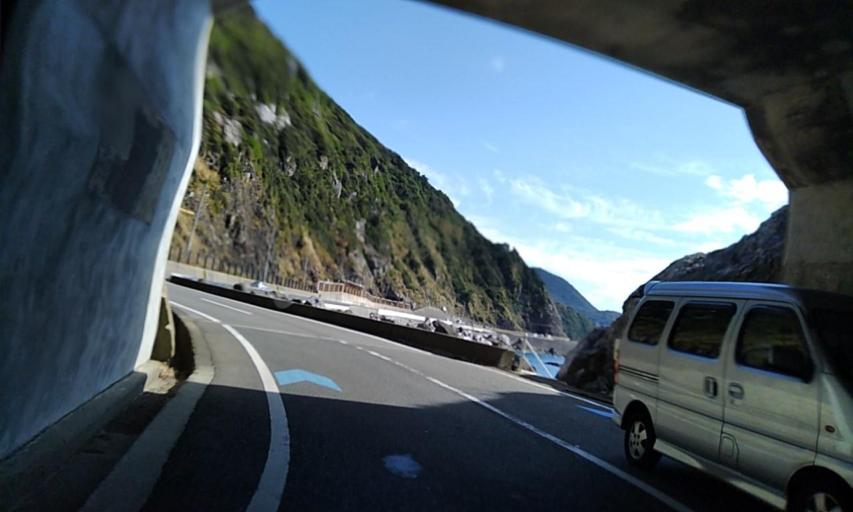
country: JP
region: Wakayama
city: Gobo
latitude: 33.9769
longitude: 135.0730
